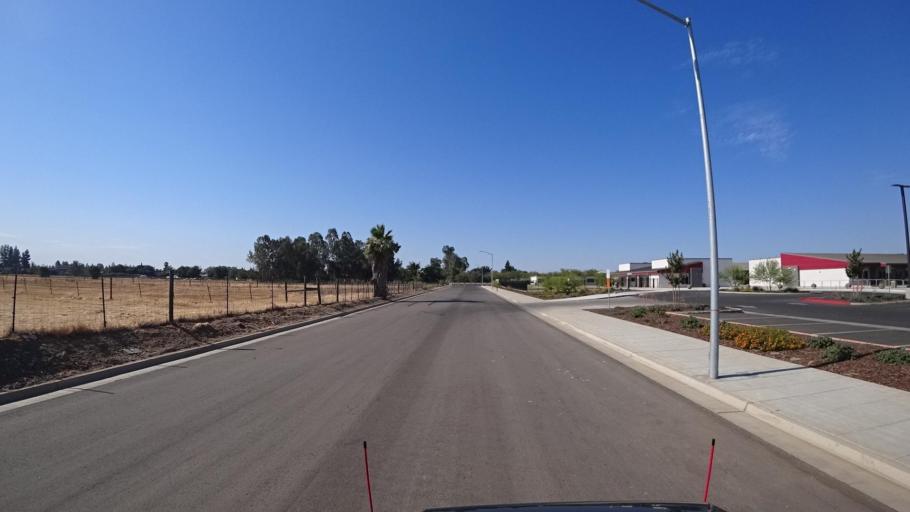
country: US
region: California
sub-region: Fresno County
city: Tarpey Village
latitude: 36.7827
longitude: -119.6506
